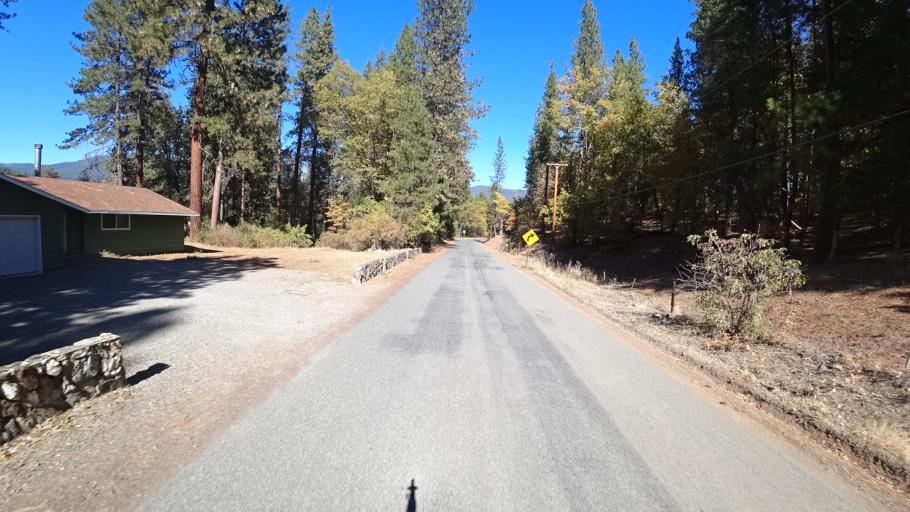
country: US
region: California
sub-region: Siskiyou County
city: Yreka
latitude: 41.6213
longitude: -122.9795
